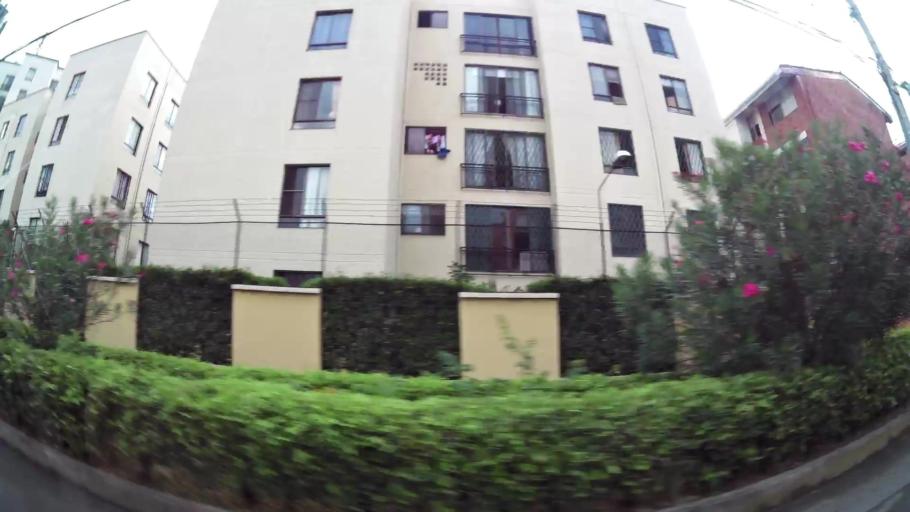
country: CO
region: Valle del Cauca
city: Cali
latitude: 3.3991
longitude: -76.5515
